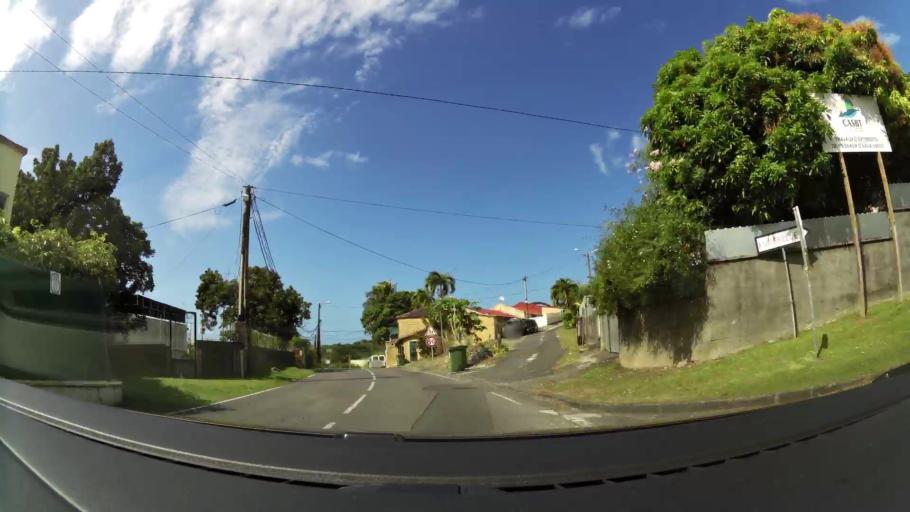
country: GP
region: Guadeloupe
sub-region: Guadeloupe
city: Saint-Claude
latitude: 16.0172
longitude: -61.7139
